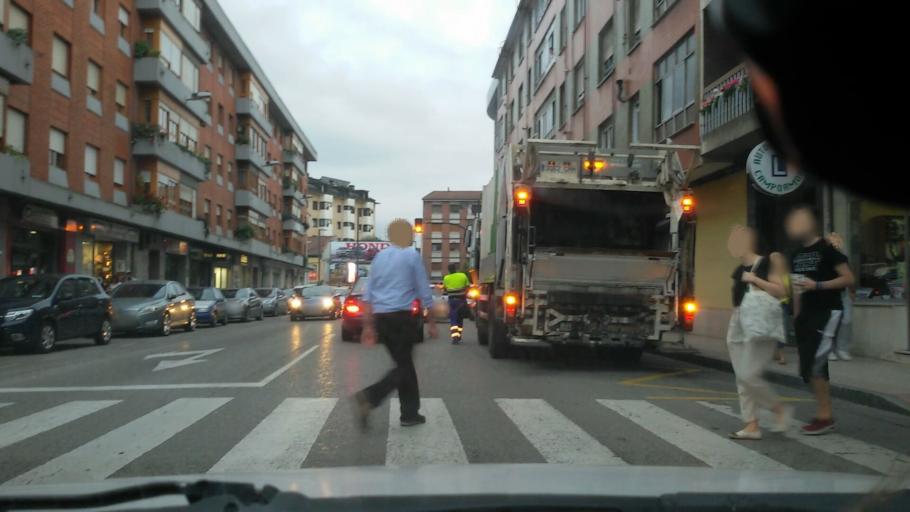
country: ES
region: Asturias
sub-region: Province of Asturias
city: Lugones
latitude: 43.4003
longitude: -5.8101
